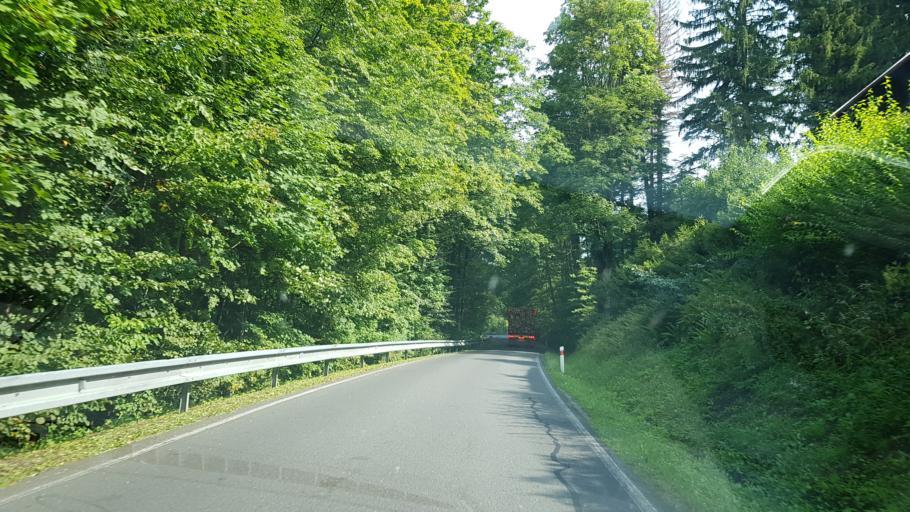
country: CZ
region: Olomoucky
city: Zlate Hory
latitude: 50.2455
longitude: 17.3558
